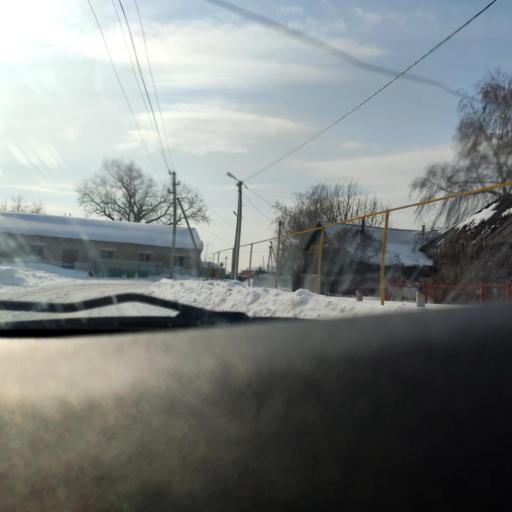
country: RU
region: Samara
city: Rozhdestveno
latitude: 53.2336
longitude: 50.0559
